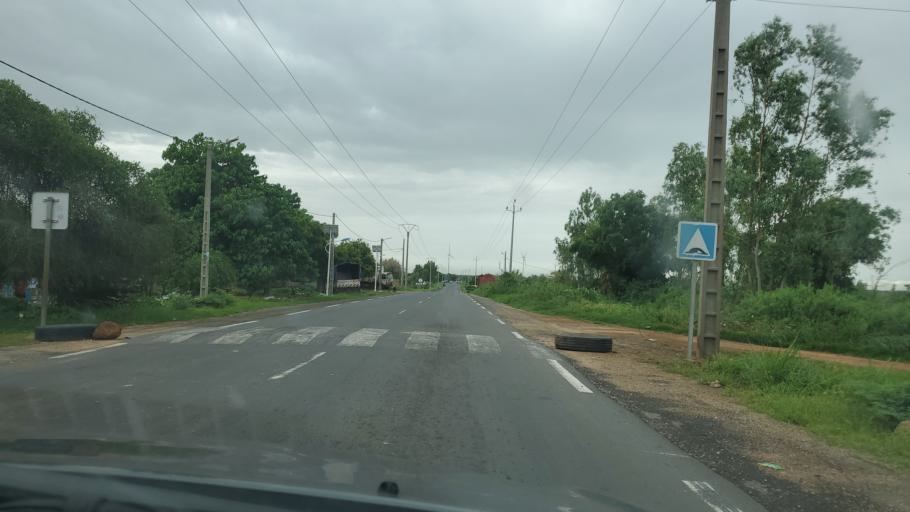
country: SN
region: Thies
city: Kayar
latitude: 15.1003
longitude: -16.9131
